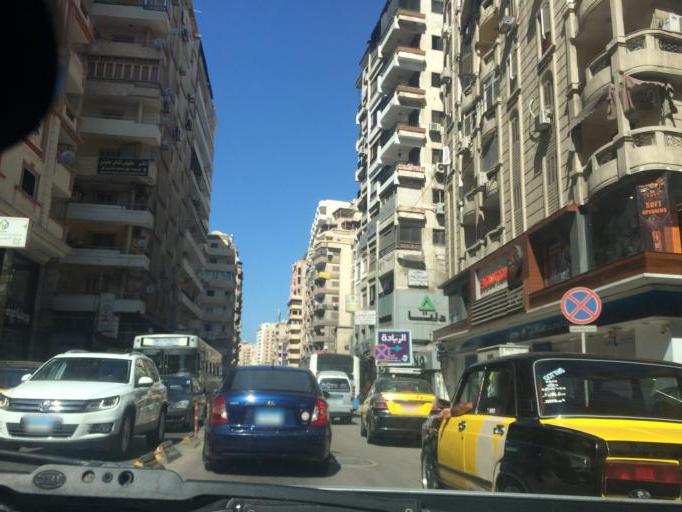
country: EG
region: Alexandria
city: Alexandria
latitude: 31.2463
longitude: 29.9756
